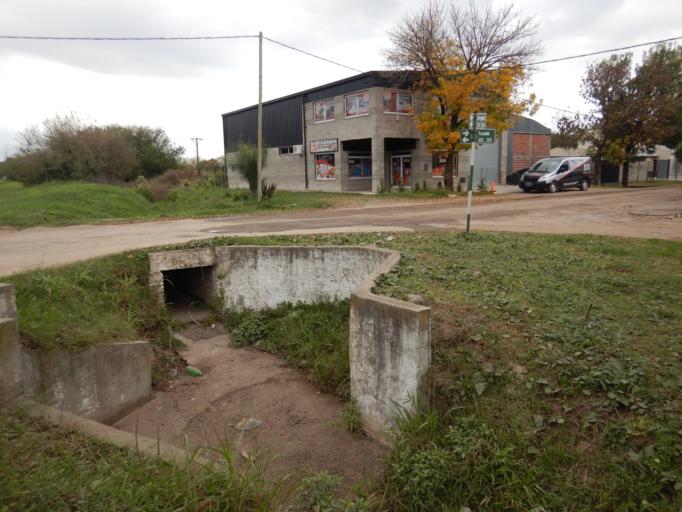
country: AR
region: Santa Fe
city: Carcarana
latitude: -32.8639
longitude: -61.1426
